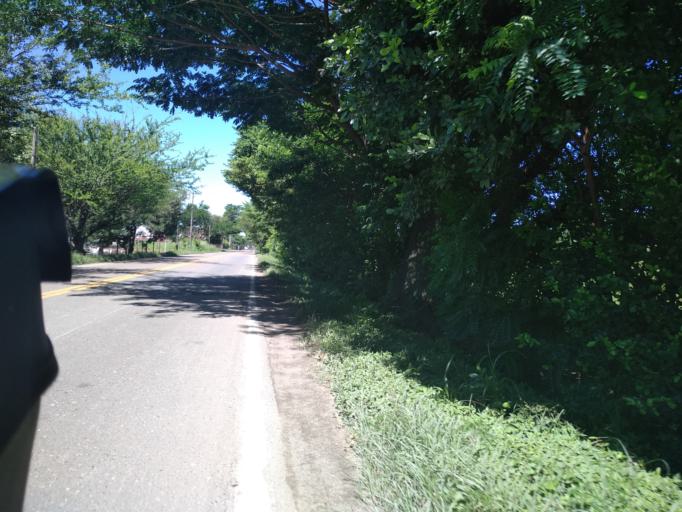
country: CO
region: Cundinamarca
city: Puerto Salgar
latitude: 5.4790
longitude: -74.6446
